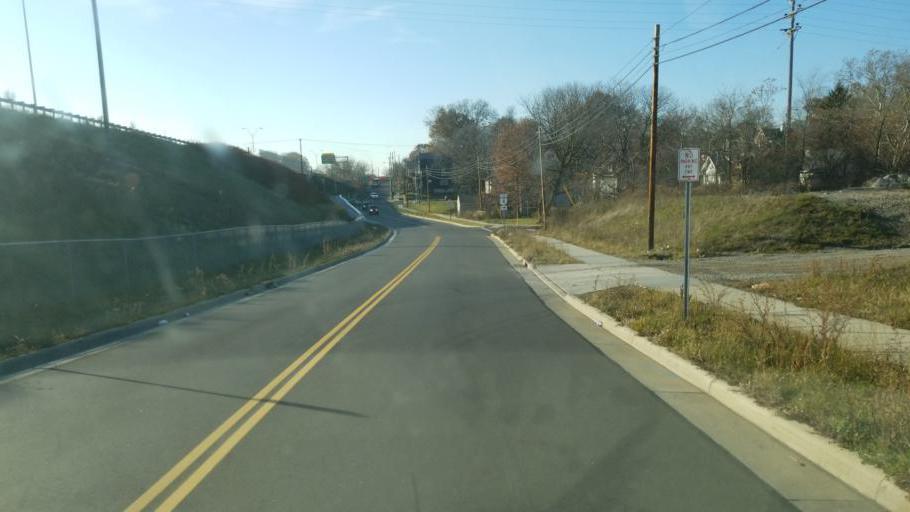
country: US
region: Ohio
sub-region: Summit County
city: Akron
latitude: 41.0628
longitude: -81.5077
